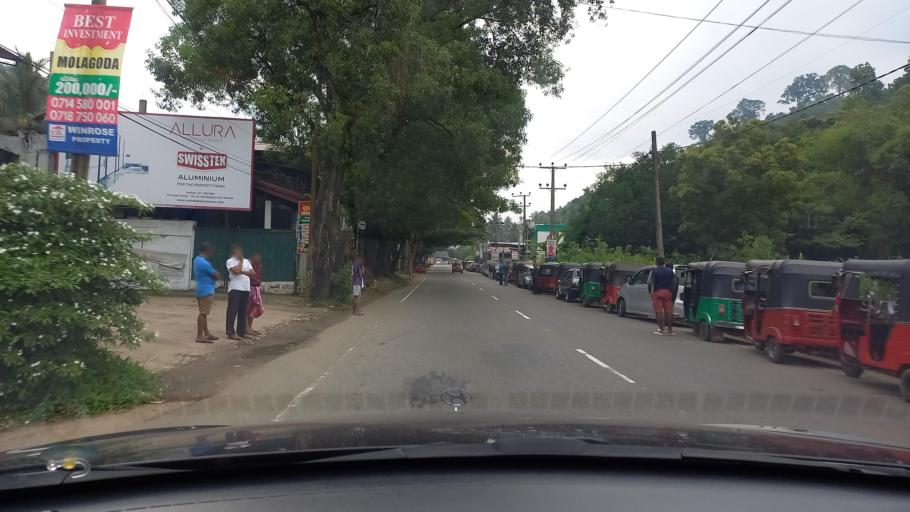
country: LK
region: Central
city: Kadugannawa
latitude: 7.2533
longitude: 80.3789
